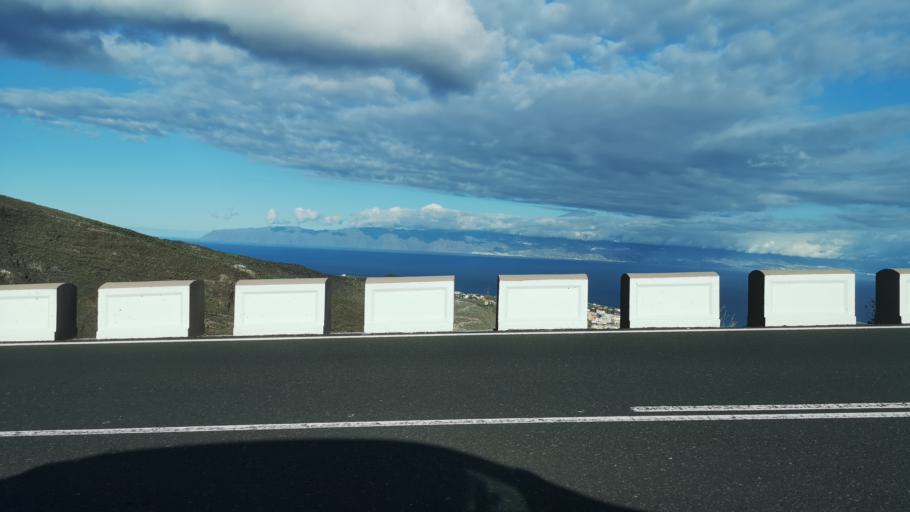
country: ES
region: Canary Islands
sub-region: Provincia de Santa Cruz de Tenerife
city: San Sebastian de la Gomera
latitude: 28.0844
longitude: -17.1369
